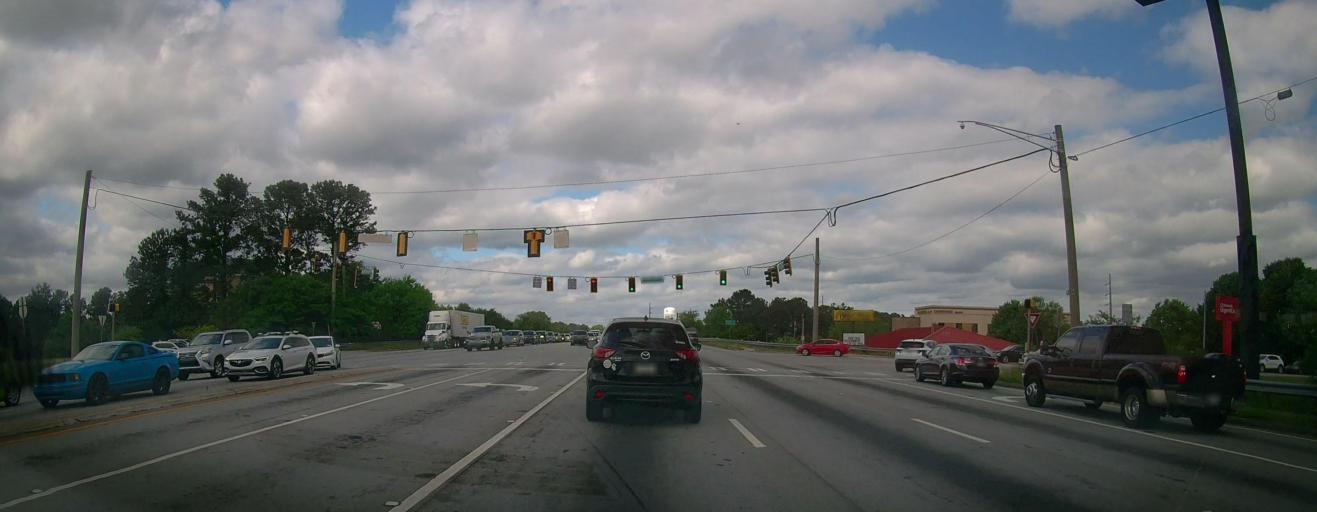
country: US
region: Georgia
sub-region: Rockdale County
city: Conyers
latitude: 33.6548
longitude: -84.0042
